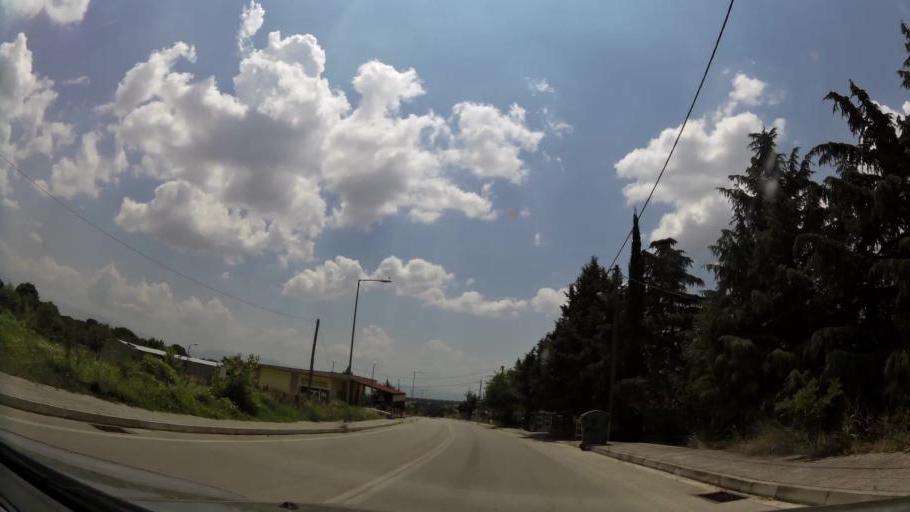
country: GR
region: West Macedonia
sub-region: Nomos Kozanis
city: Kozani
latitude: 40.2884
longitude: 21.7983
